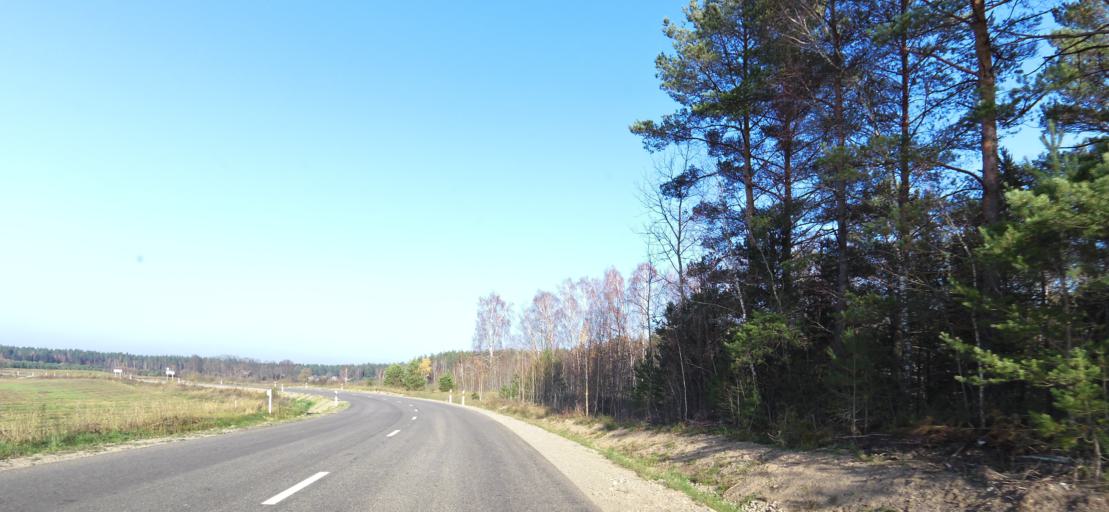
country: LT
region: Vilnius County
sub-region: Trakai
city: Rudiskes
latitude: 54.5100
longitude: 24.8637
